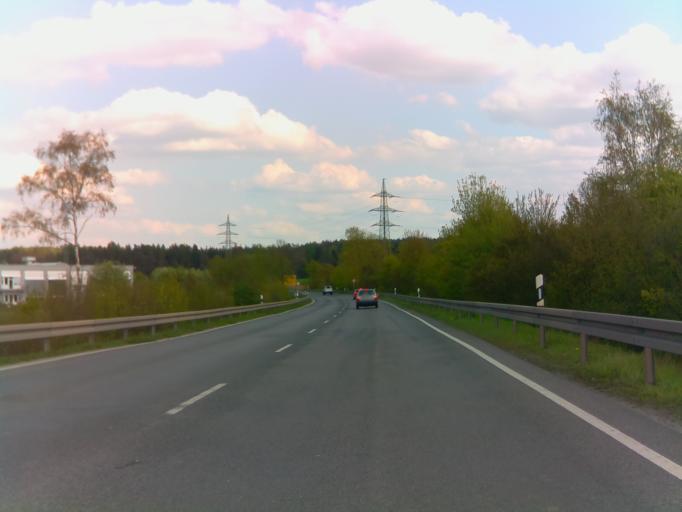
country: DE
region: Bavaria
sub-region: Upper Franconia
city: Neustadt bei Coburg
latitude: 50.3115
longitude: 11.1018
